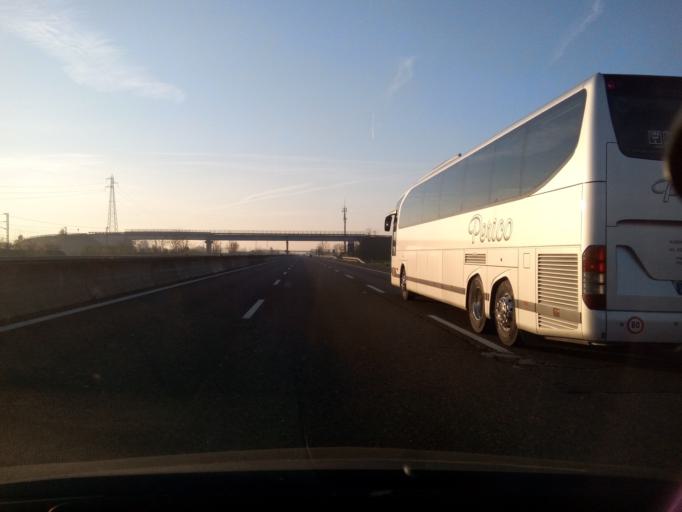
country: IT
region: Lombardy
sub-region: Provincia di Lodi
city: Borghetto Lodigiano
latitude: 45.2255
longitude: 9.5164
